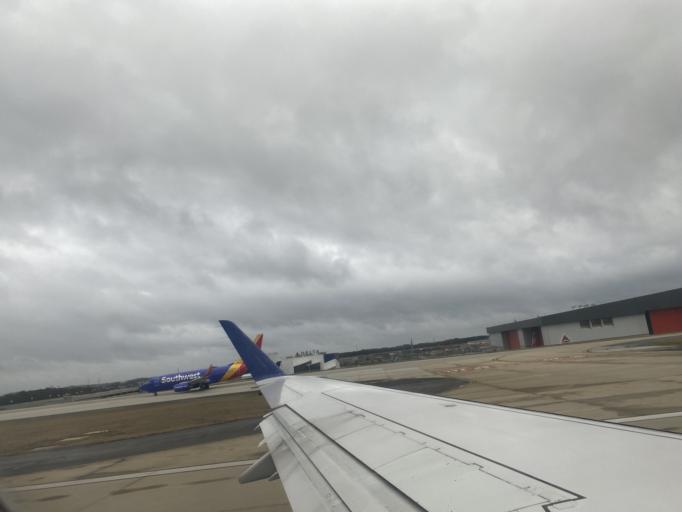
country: US
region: Georgia
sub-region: Fulton County
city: Hapeville
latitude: 33.6468
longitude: -84.4074
